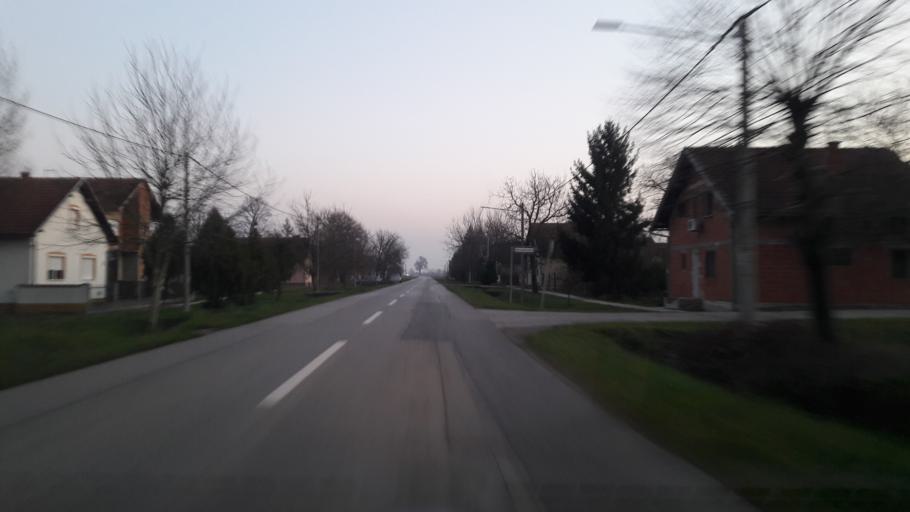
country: HR
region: Vukovarsko-Srijemska
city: Nijemci
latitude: 45.1768
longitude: 19.0129
